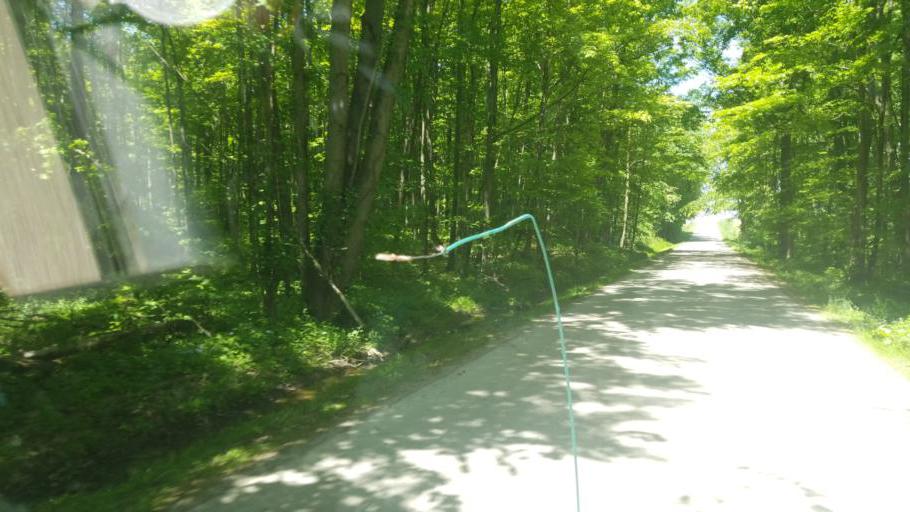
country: US
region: Ohio
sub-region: Huron County
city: Greenwich
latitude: 40.9847
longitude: -82.4322
